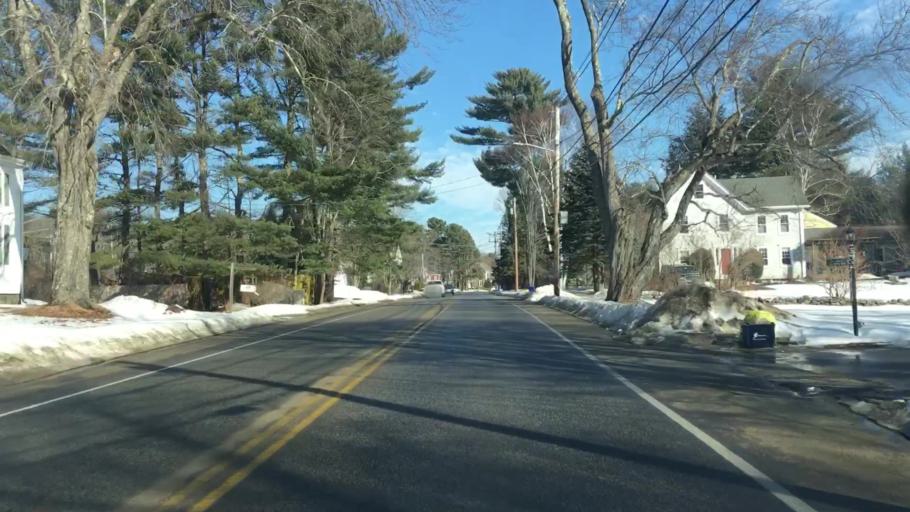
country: US
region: Maine
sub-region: Cumberland County
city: Falmouth
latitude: 43.7276
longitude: -70.2426
